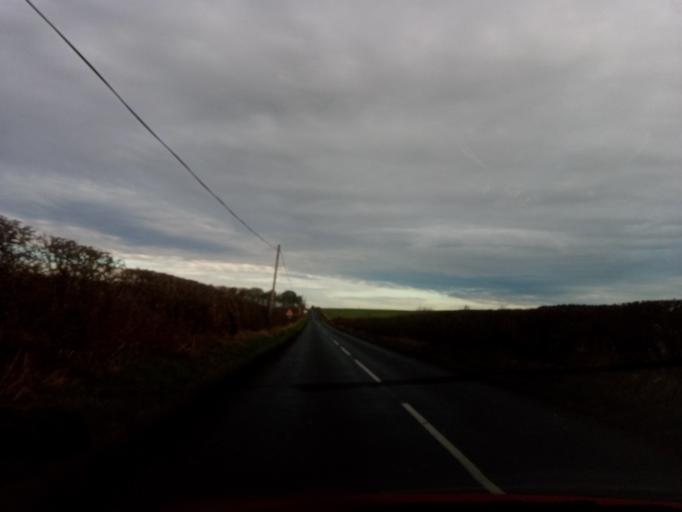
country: GB
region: Scotland
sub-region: The Scottish Borders
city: Coldstream
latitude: 55.6765
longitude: -2.2327
